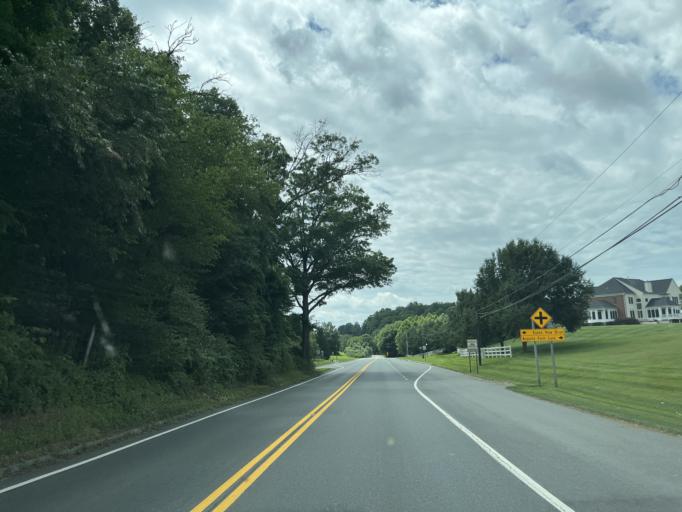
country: US
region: Maryland
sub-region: Montgomery County
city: Montgomery Village
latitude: 39.2242
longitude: -77.1764
